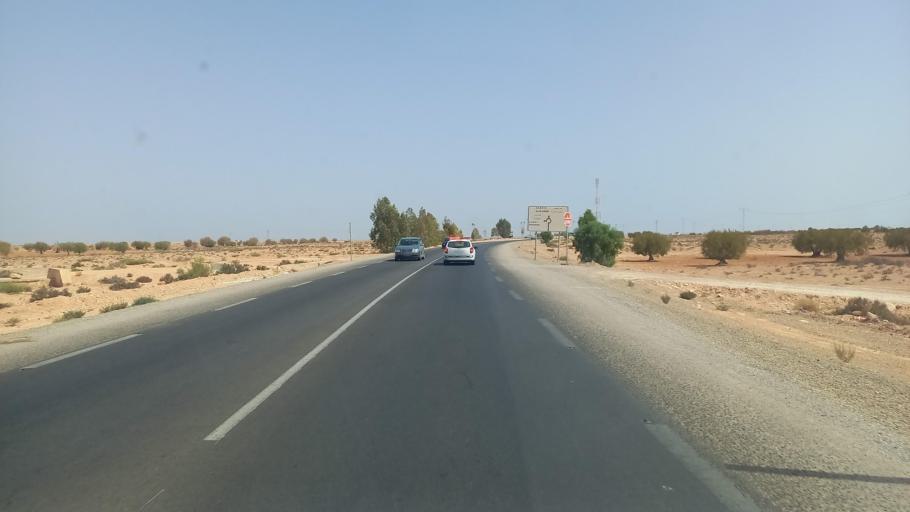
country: TN
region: Madanin
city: Medenine
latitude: 33.3825
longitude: 10.6998
